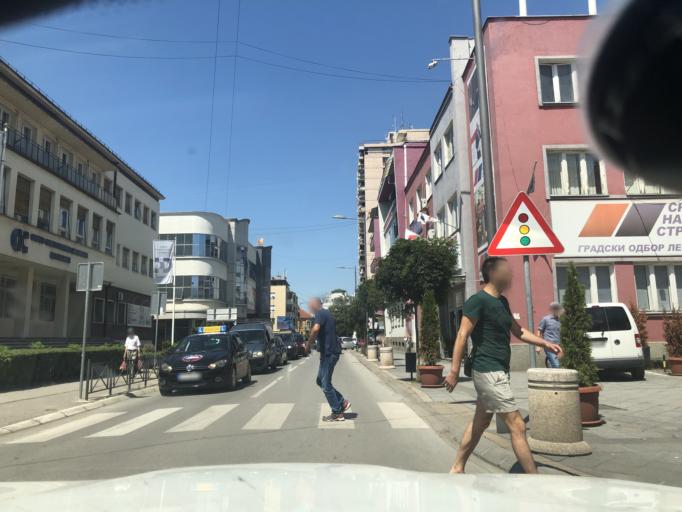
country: RS
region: Central Serbia
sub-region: Jablanicki Okrug
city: Leskovac
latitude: 42.9953
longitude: 21.9480
